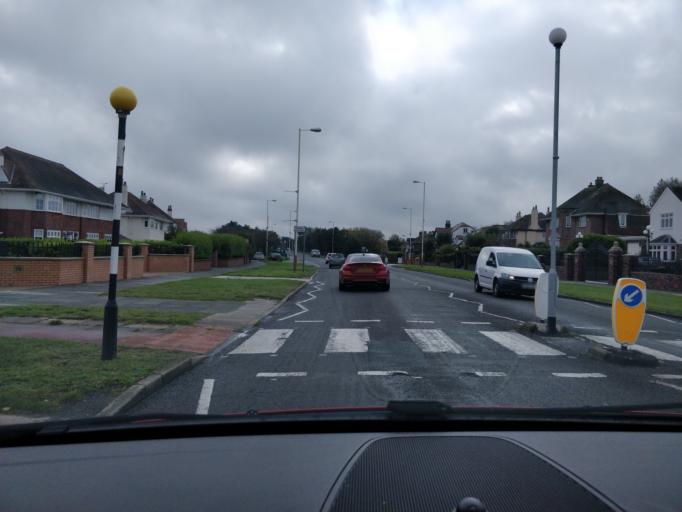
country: GB
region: England
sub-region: Sefton
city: Southport
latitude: 53.6243
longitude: -3.0273
